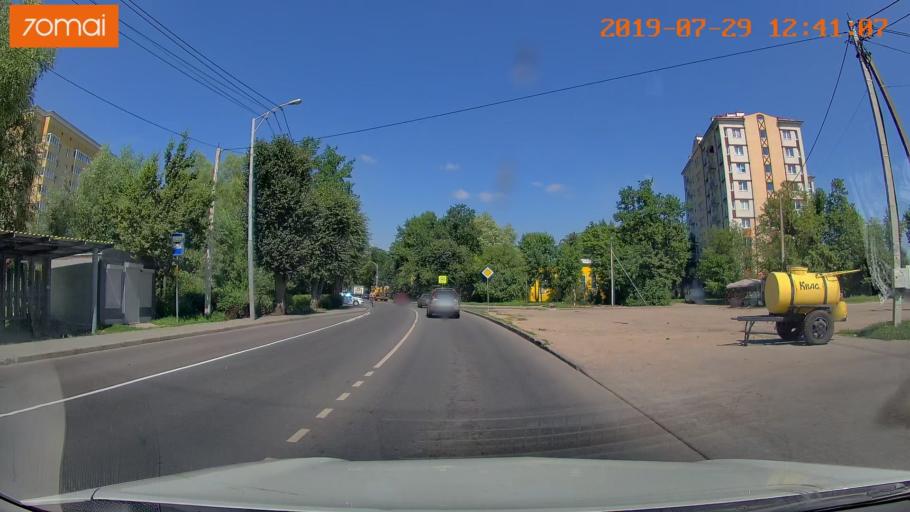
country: RU
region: Kaliningrad
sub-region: Gorod Kaliningrad
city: Kaliningrad
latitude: 54.6709
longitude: 20.5456
